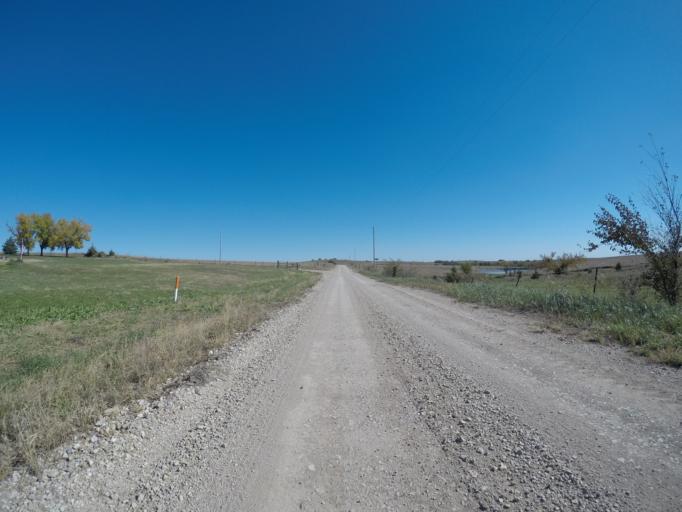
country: US
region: Kansas
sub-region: Wabaunsee County
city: Alma
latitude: 39.0435
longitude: -96.3590
